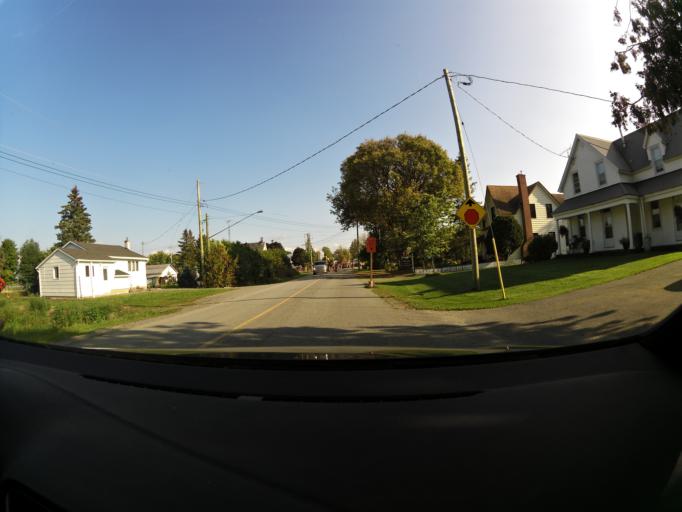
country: CA
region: Ontario
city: Arnprior
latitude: 45.3927
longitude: -76.1899
